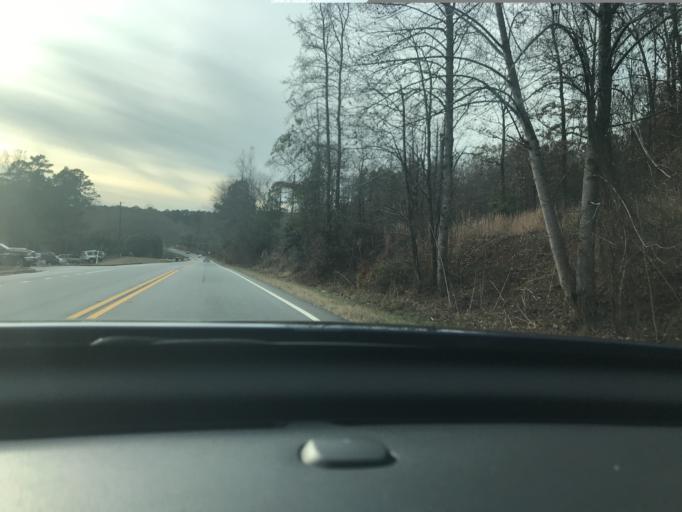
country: US
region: Georgia
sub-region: Newton County
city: Porterdale
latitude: 33.5837
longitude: -83.9167
